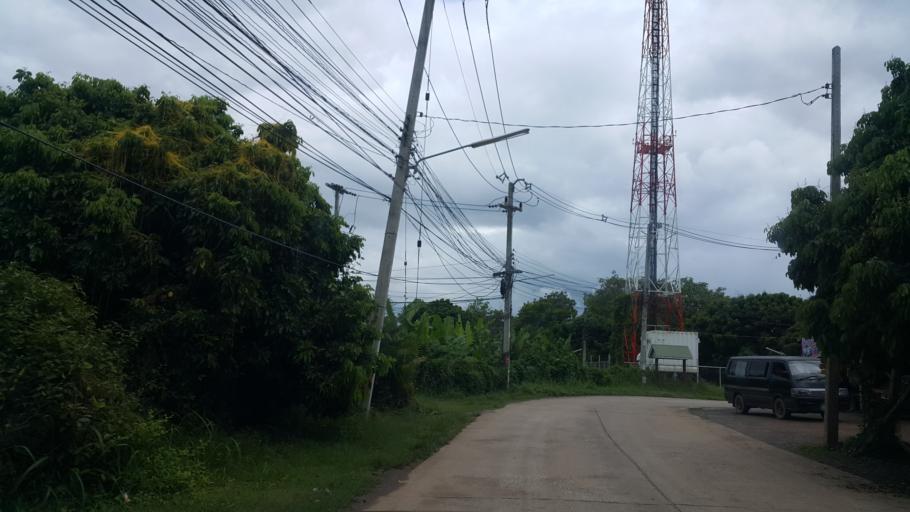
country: TH
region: Sukhothai
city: Thung Saliam
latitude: 17.3204
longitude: 99.5650
